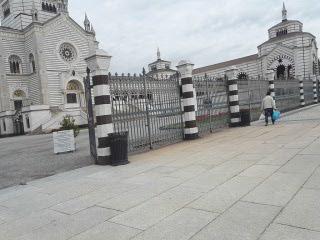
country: IT
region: Lombardy
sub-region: Citta metropolitana di Milano
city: Milano
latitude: 45.4849
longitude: 9.1790
